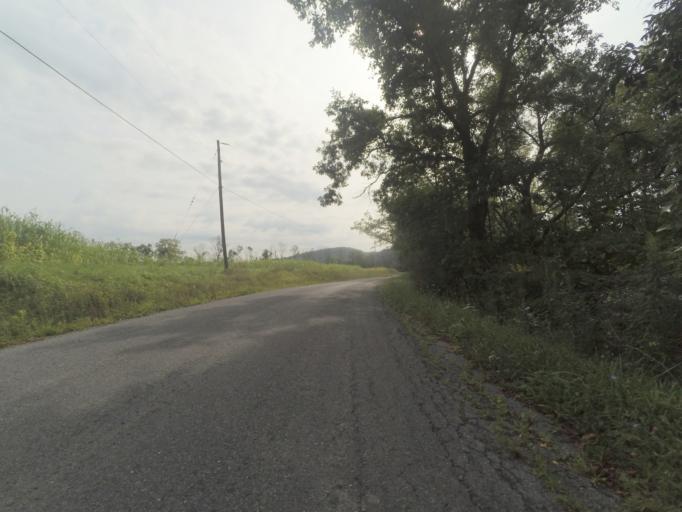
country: US
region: Pennsylvania
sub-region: Huntingdon County
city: McConnellstown
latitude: 40.5237
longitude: -78.1021
